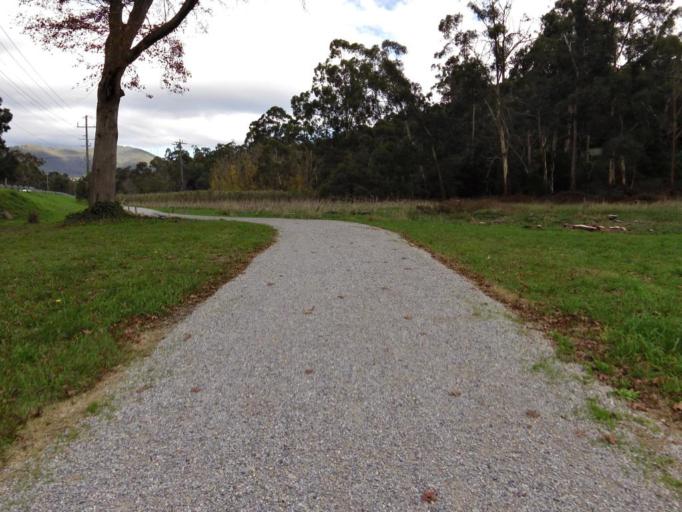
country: AU
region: Victoria
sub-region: Yarra Ranges
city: Mount Evelyn
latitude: -37.7845
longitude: 145.3617
